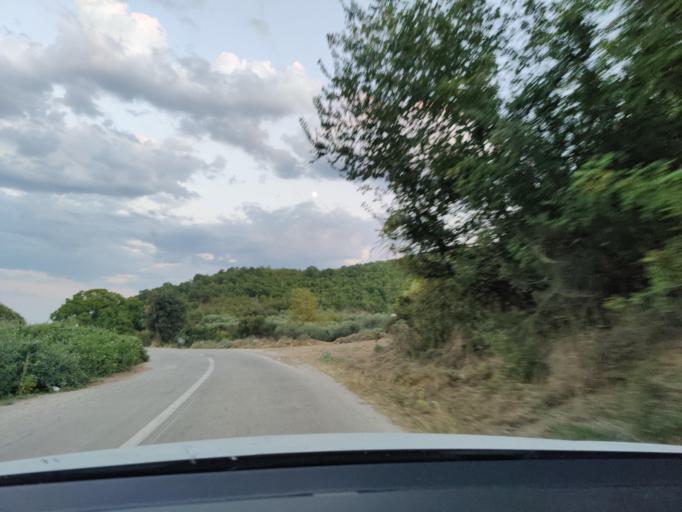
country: GR
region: Central Macedonia
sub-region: Nomos Serron
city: Chrysochorafa
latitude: 41.1630
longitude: 23.1837
